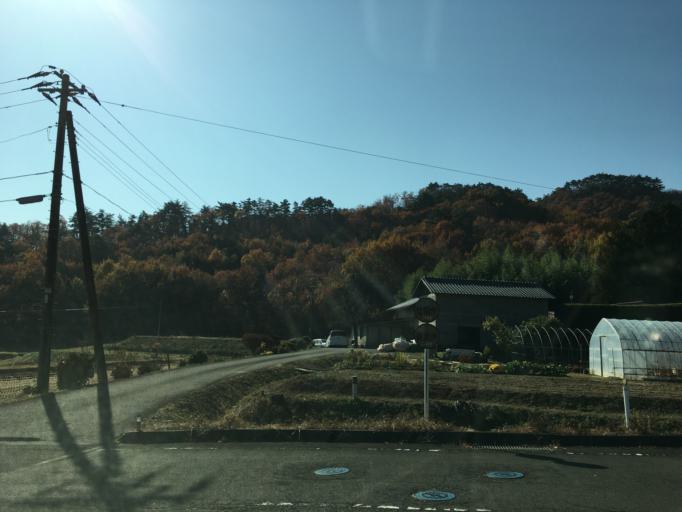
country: JP
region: Fukushima
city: Nihommatsu
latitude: 37.5745
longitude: 140.3722
